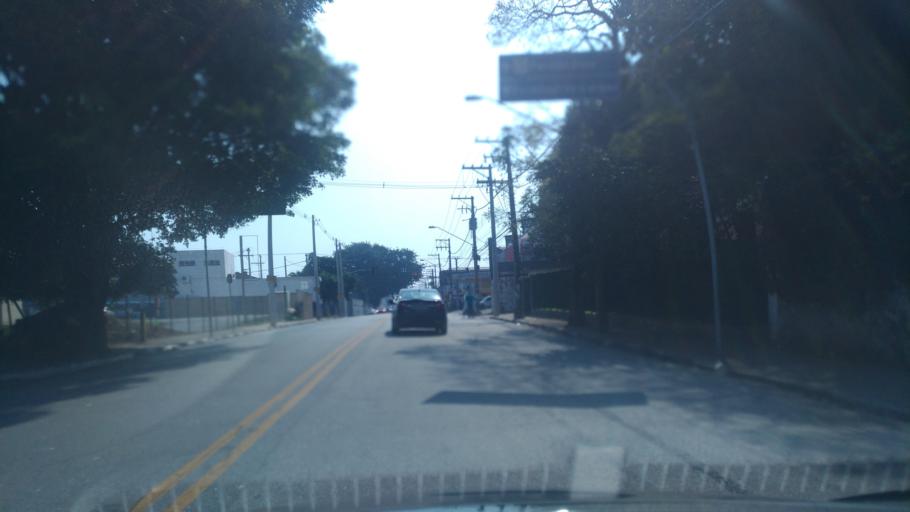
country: BR
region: Sao Paulo
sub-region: Guarulhos
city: Guarulhos
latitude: -23.4859
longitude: -46.5501
